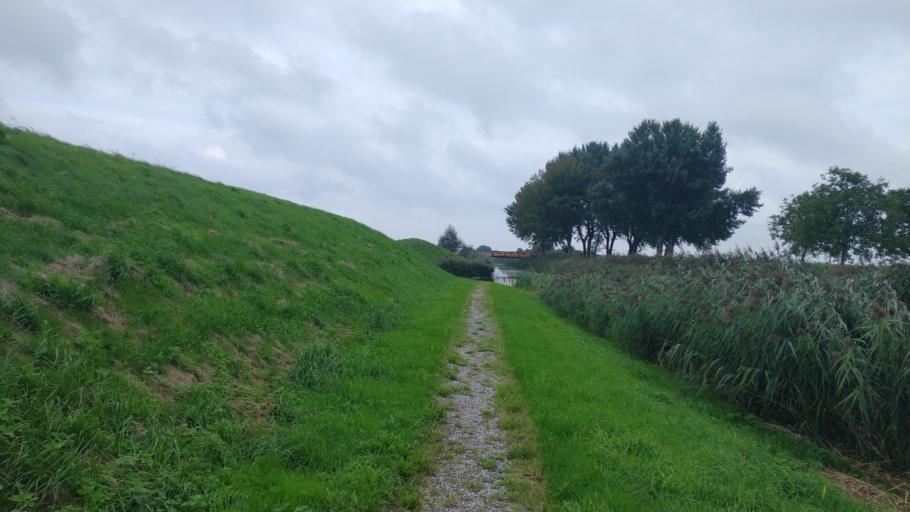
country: NL
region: Flevoland
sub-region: Gemeente Zeewolde
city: Zeewolde
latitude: 52.3967
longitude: 5.4537
